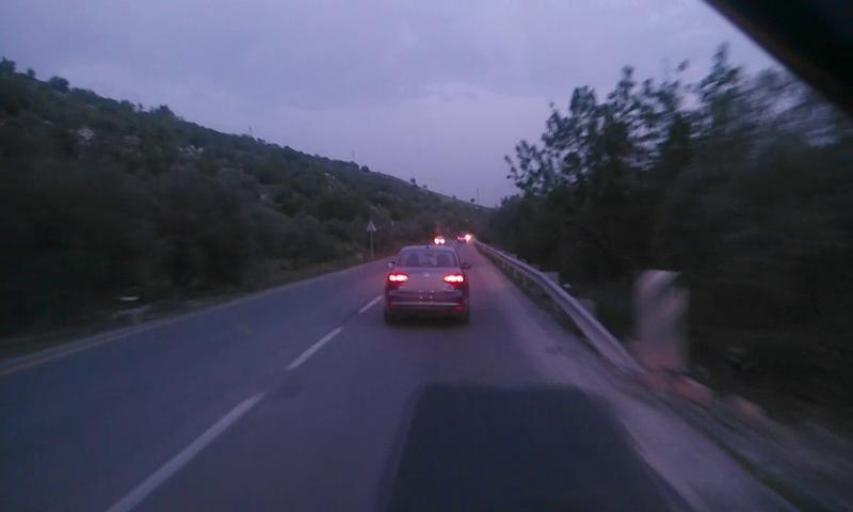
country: PS
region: West Bank
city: Ramin
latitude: 32.2838
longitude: 35.1408
